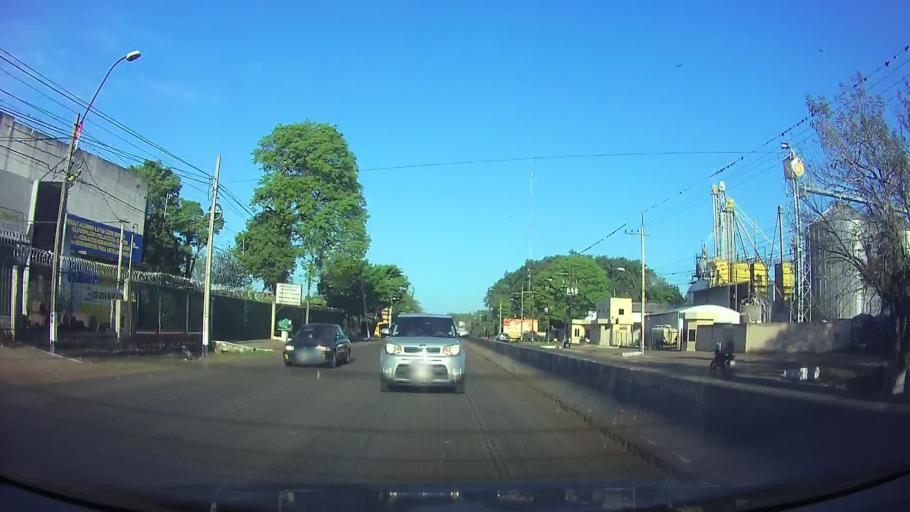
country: PY
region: Central
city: Capiata
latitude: -25.3476
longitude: -57.4674
